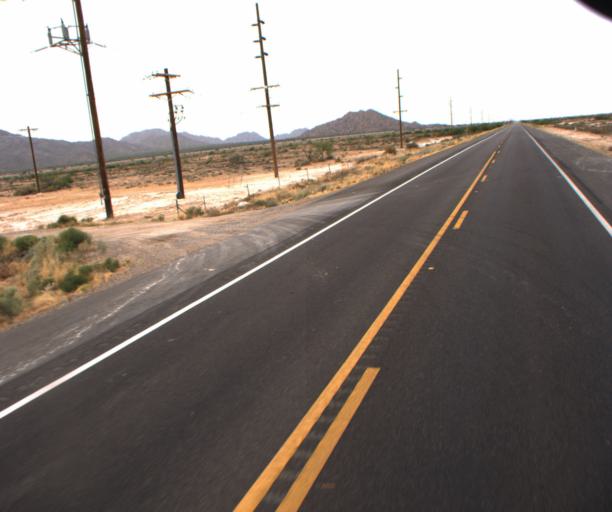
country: US
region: Arizona
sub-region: Pinal County
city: Blackwater
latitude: 33.0072
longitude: -111.6170
